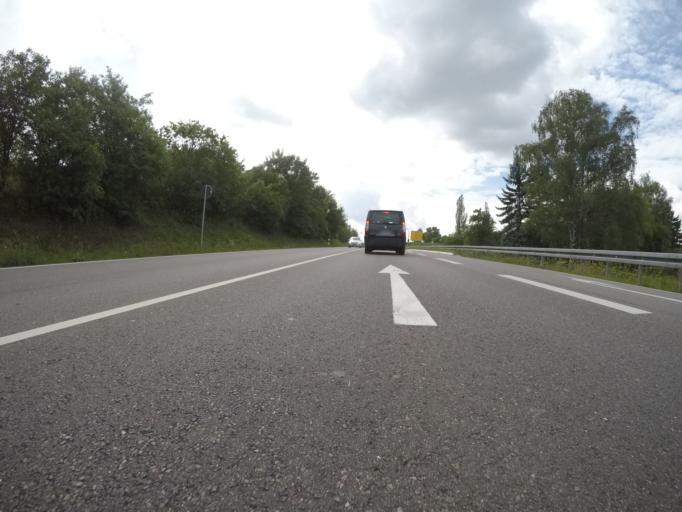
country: DE
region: Baden-Wuerttemberg
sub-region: Regierungsbezirk Stuttgart
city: Nufringen
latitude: 48.6149
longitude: 8.8843
